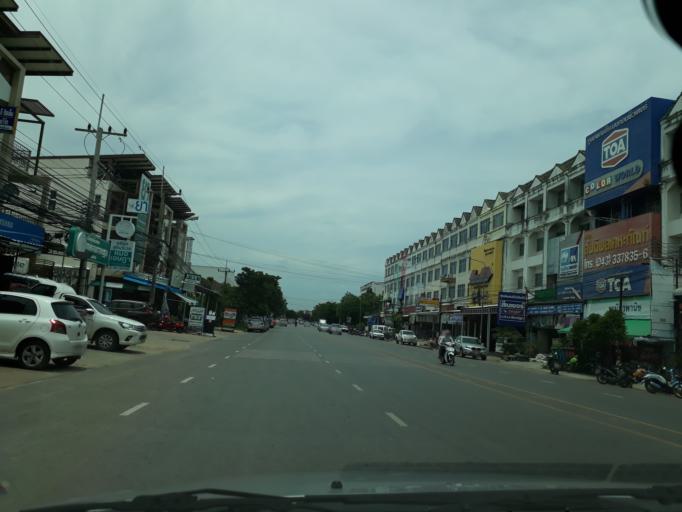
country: TH
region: Khon Kaen
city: Khon Kaen
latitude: 16.4338
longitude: 102.8627
